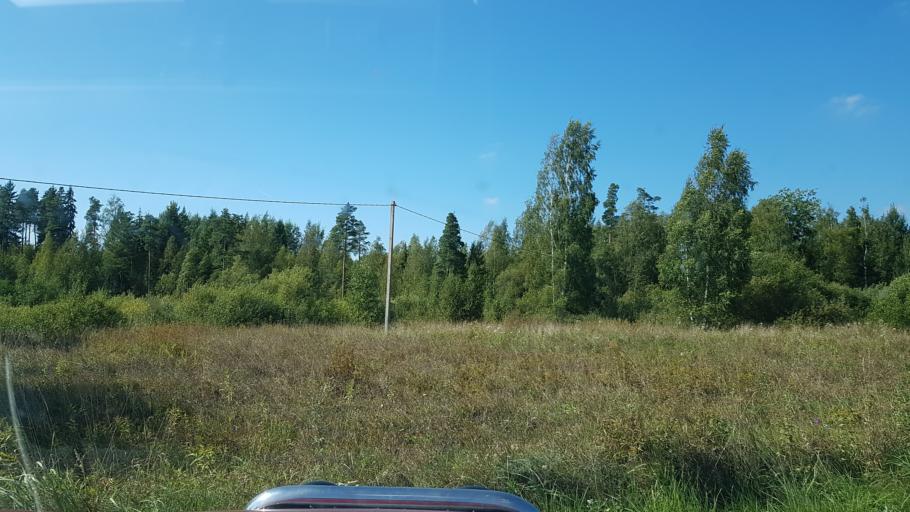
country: EE
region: Polvamaa
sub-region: Raepina vald
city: Rapina
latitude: 58.1425
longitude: 27.3857
